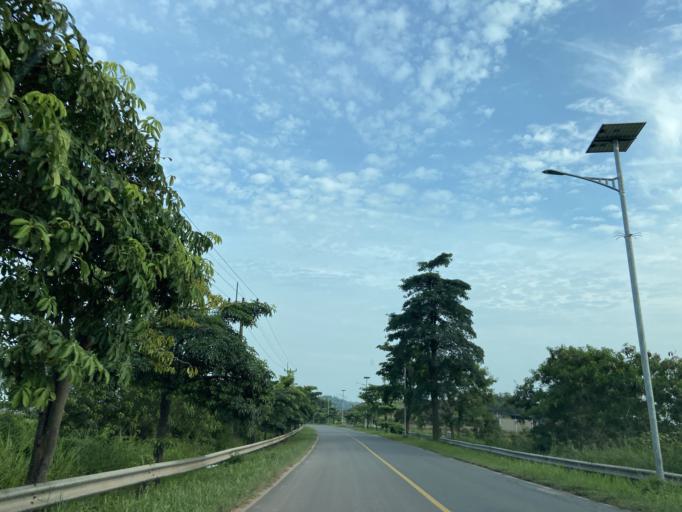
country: ID
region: Riau Islands
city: Tanjungpinang
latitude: 0.9293
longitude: 104.1134
